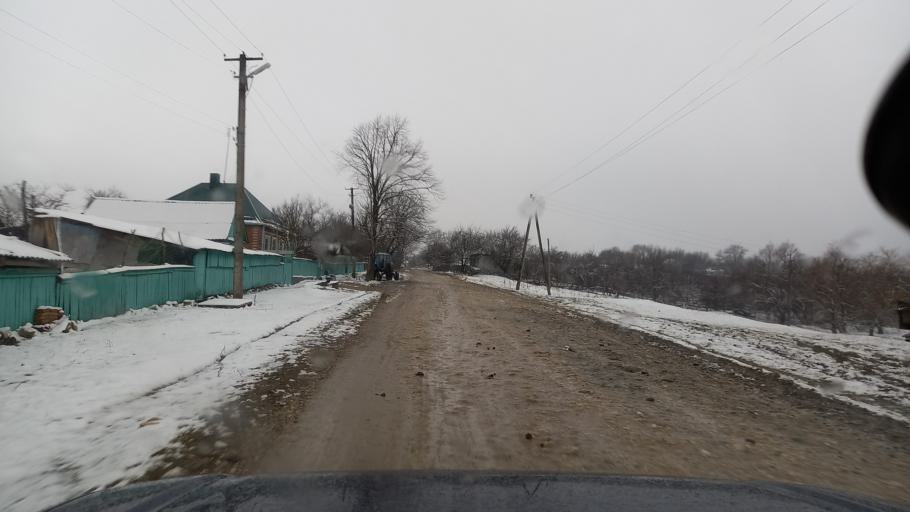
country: RU
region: Adygeya
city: Abadzekhskaya
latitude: 44.3603
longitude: 40.4097
